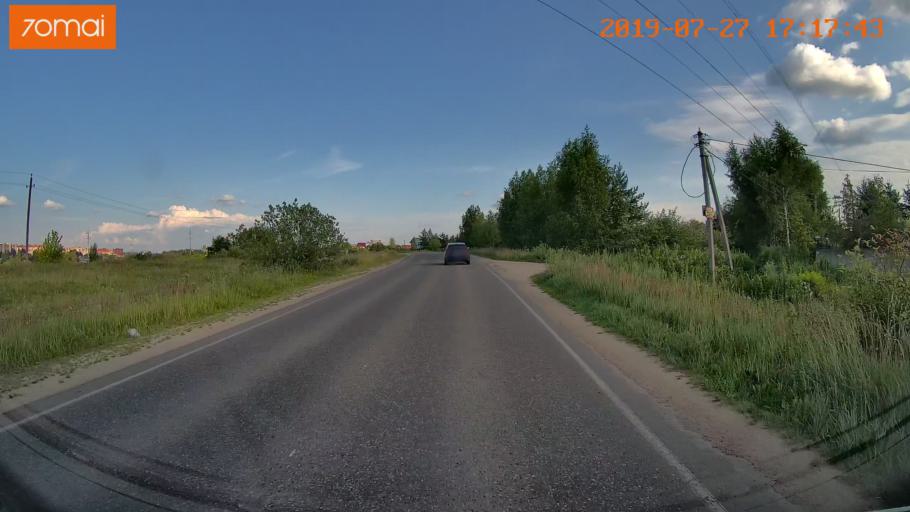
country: RU
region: Ivanovo
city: Novo-Talitsy
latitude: 57.0349
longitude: 40.8977
